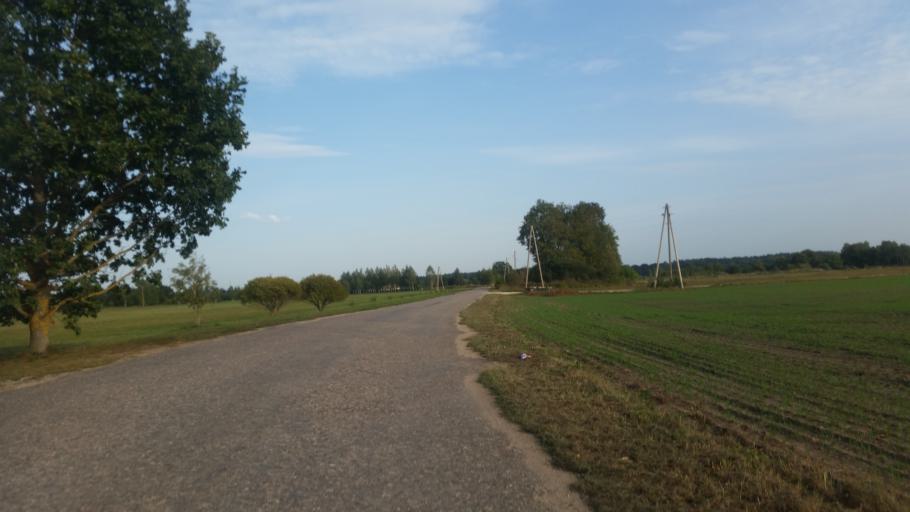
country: LV
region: Ikskile
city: Ikskile
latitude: 56.8186
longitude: 24.5389
